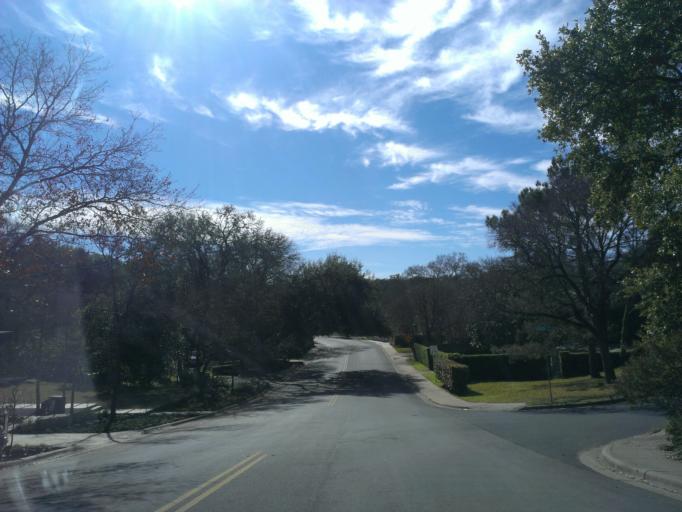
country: US
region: Texas
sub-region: Travis County
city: West Lake Hills
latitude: 30.3062
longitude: -97.7698
